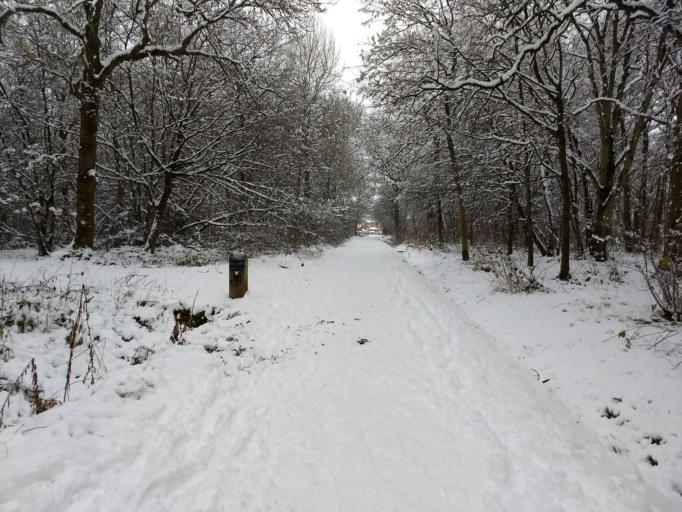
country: GB
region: England
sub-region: Milton Keynes
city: Shenley Church End
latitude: 52.0004
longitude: -0.7856
